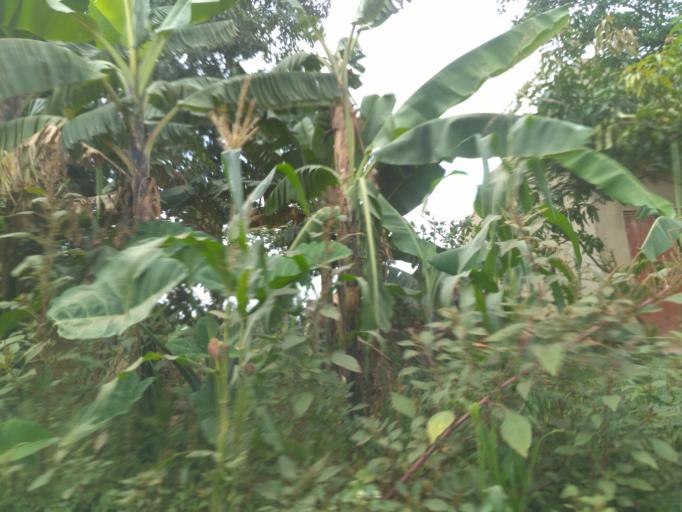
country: UG
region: Central Region
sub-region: Wakiso District
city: Bweyogerere
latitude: 0.4685
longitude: 32.6230
